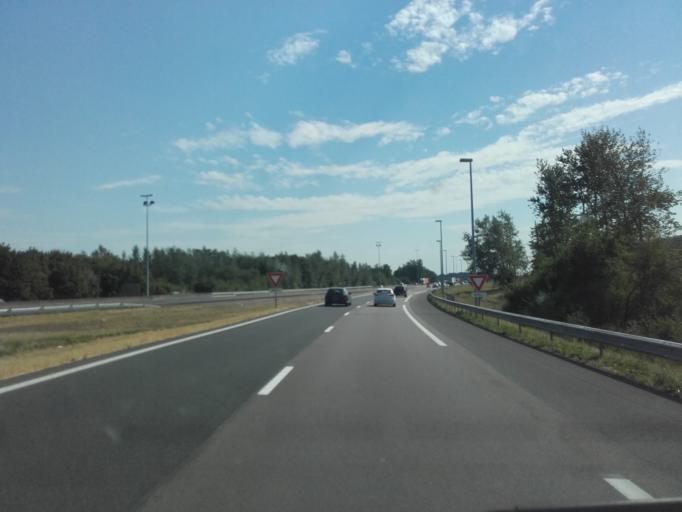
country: FR
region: Bourgogne
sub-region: Departement de la Cote-d'Or
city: Beaune
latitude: 47.0259
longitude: 4.8725
